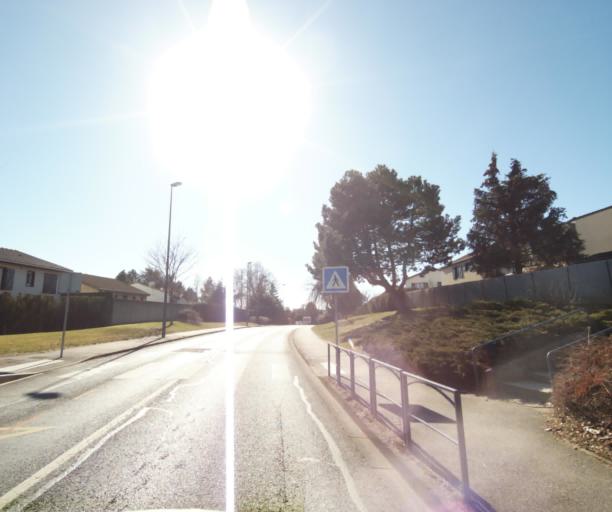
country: FR
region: Lorraine
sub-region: Departement de Meurthe-et-Moselle
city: Heillecourt
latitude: 48.6605
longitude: 6.2001
